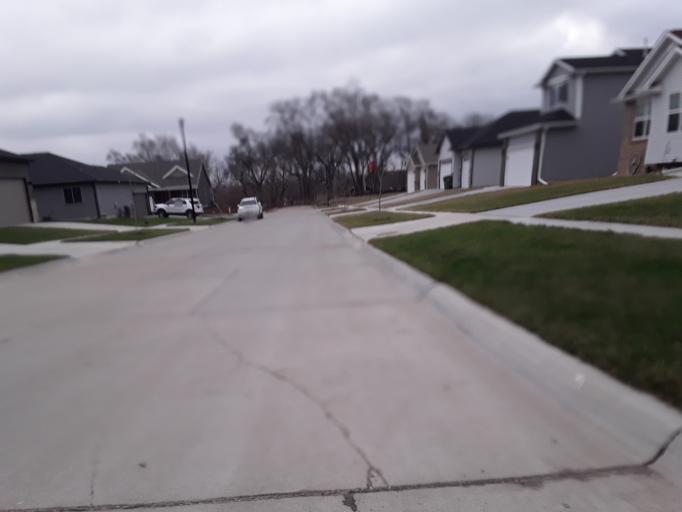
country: US
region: Nebraska
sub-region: Lancaster County
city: Lincoln
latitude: 40.8430
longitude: -96.5931
